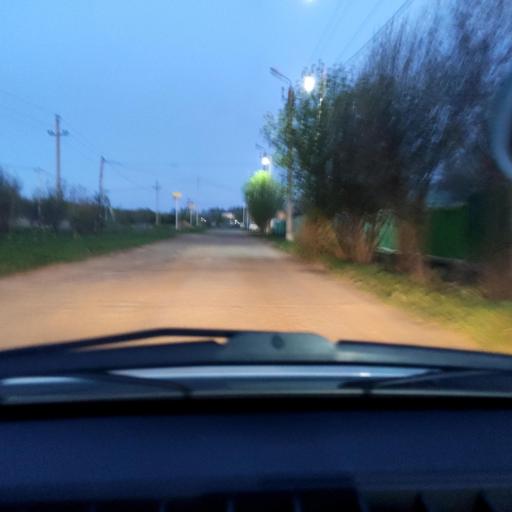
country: RU
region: Bashkortostan
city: Mikhaylovka
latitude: 54.8649
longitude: 55.7455
